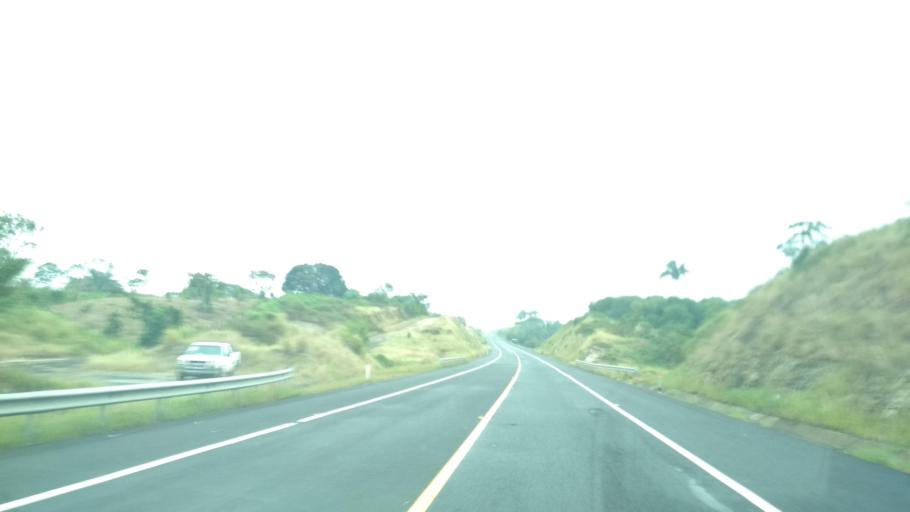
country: MX
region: Veracruz
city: Vega de San Marcos
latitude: 20.1800
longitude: -96.9648
